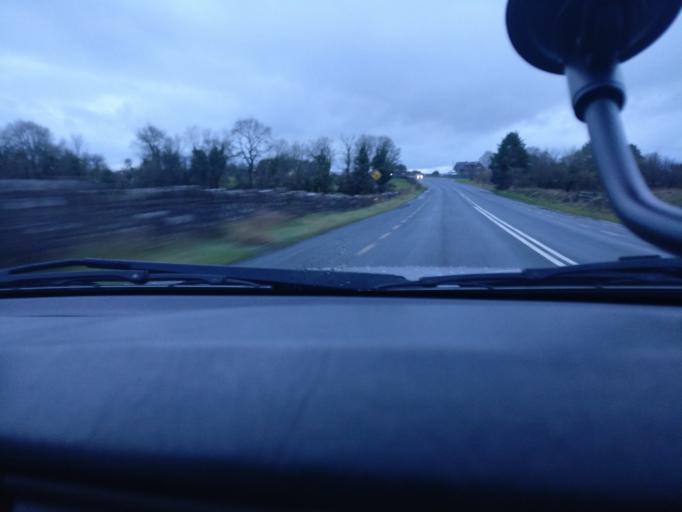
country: IE
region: Connaught
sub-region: County Galway
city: Loughrea
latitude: 53.2589
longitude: -8.4344
